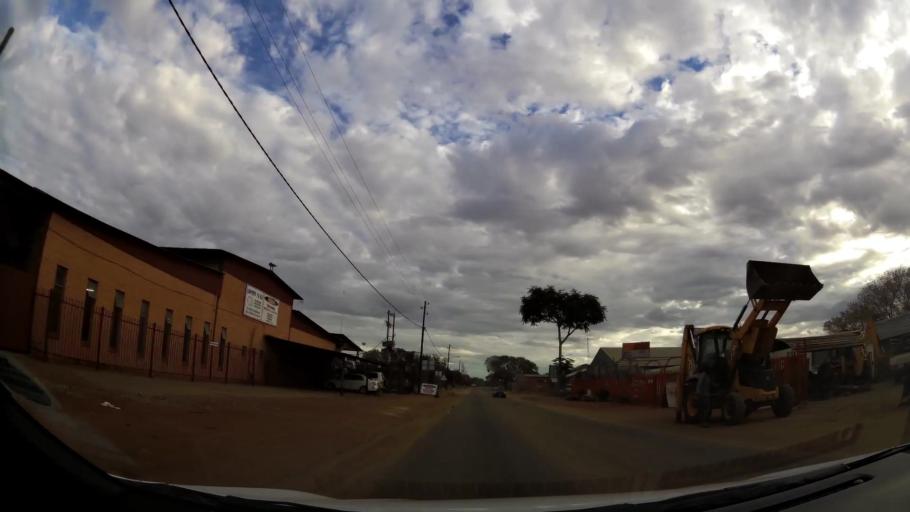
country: ZA
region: Limpopo
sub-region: Waterberg District Municipality
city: Modimolle
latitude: -24.5247
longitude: 28.7124
